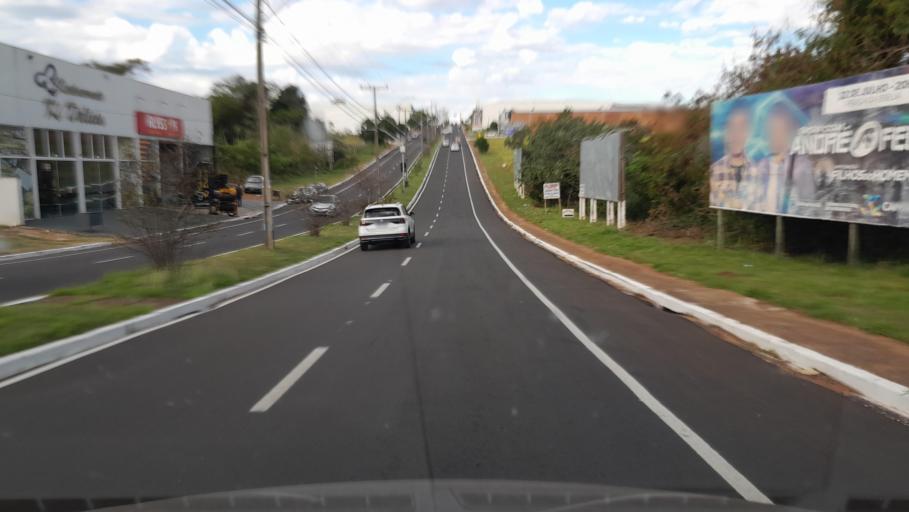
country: BR
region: Parana
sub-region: Umuarama
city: Umuarama
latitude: -23.7540
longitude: -53.2792
